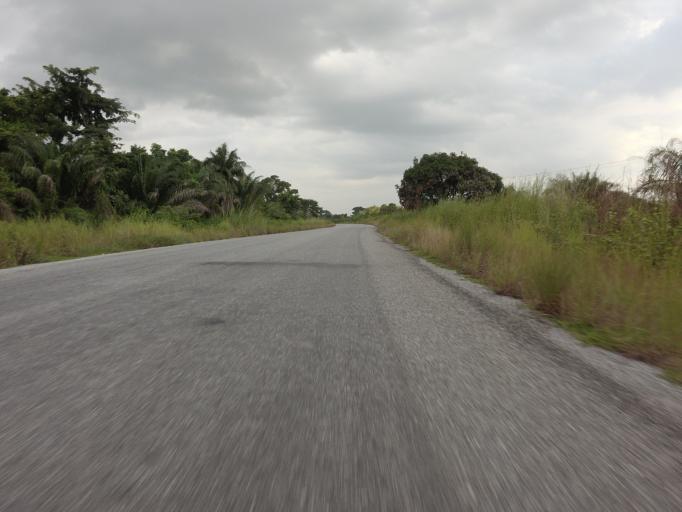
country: GH
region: Volta
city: Ho
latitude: 6.4769
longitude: 0.4958
